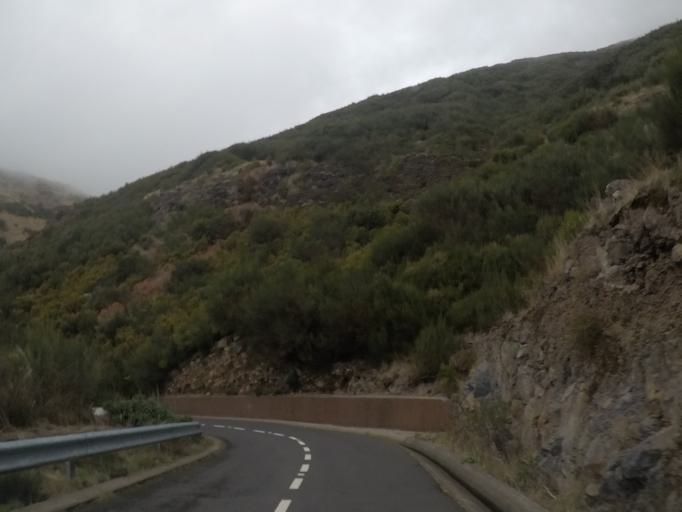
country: PT
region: Madeira
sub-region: Camara de Lobos
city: Curral das Freiras
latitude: 32.7240
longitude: -16.9271
